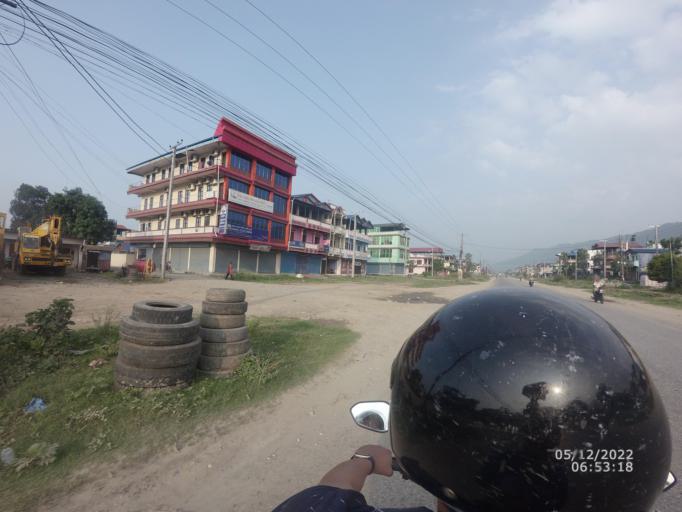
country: NP
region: Central Region
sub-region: Narayani Zone
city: Bharatpur
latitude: 27.7056
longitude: 84.3935
